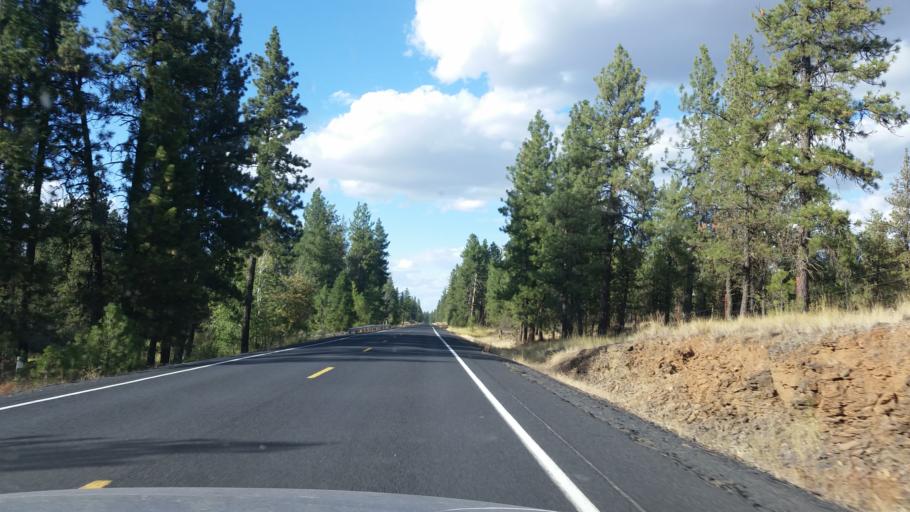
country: US
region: Washington
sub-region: Spokane County
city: Cheney
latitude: 47.4118
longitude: -117.5686
